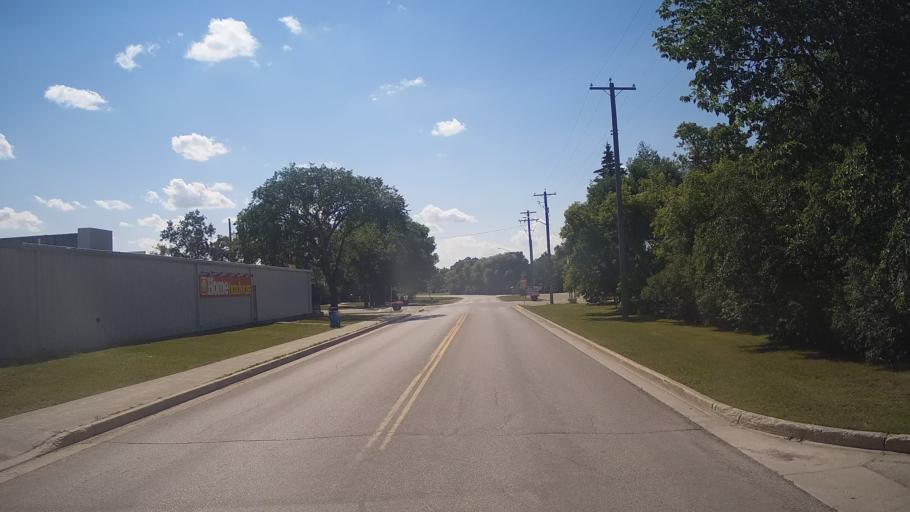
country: CA
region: Manitoba
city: Stonewall
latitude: 50.1313
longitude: -97.3251
